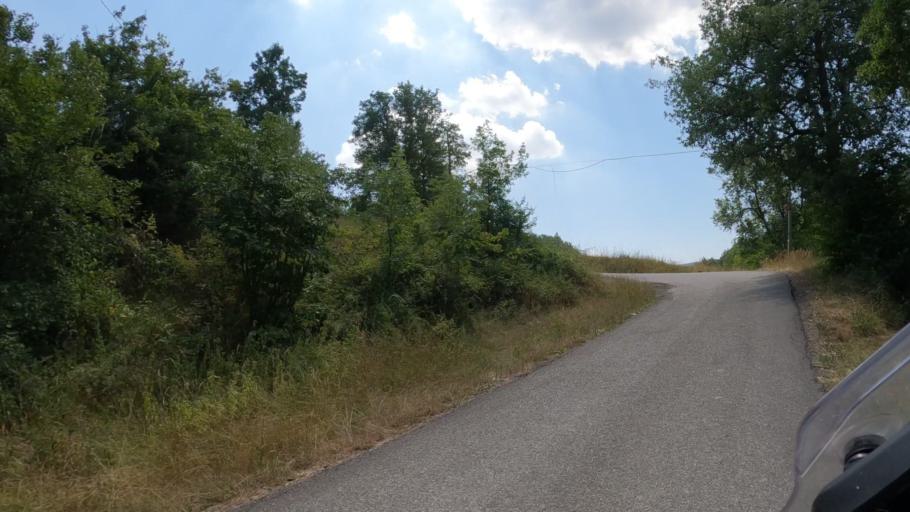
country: IT
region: Piedmont
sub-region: Provincia di Alessandria
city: Cassinelle-Concentrico
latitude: 44.5711
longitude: 8.5575
